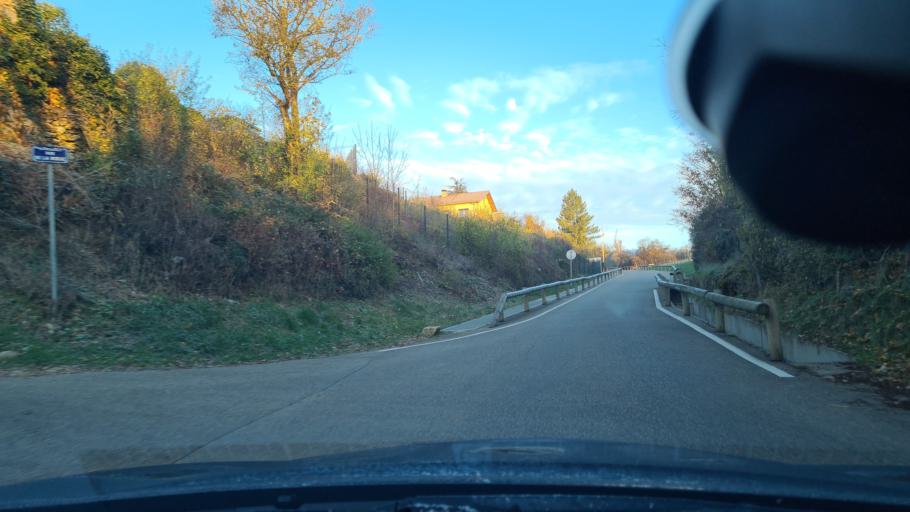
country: FR
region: Rhone-Alpes
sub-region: Departement du Rhone
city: Limonest
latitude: 45.8274
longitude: 4.7964
